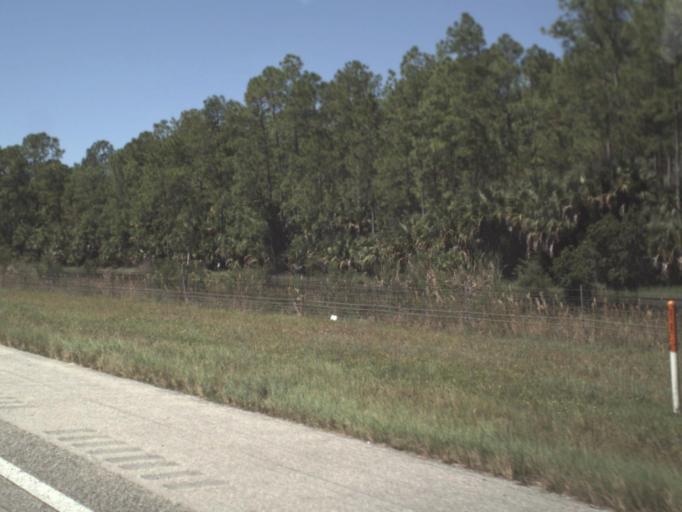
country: US
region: Florida
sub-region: Collier County
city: Golden Gate
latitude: 26.1549
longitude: -81.6403
